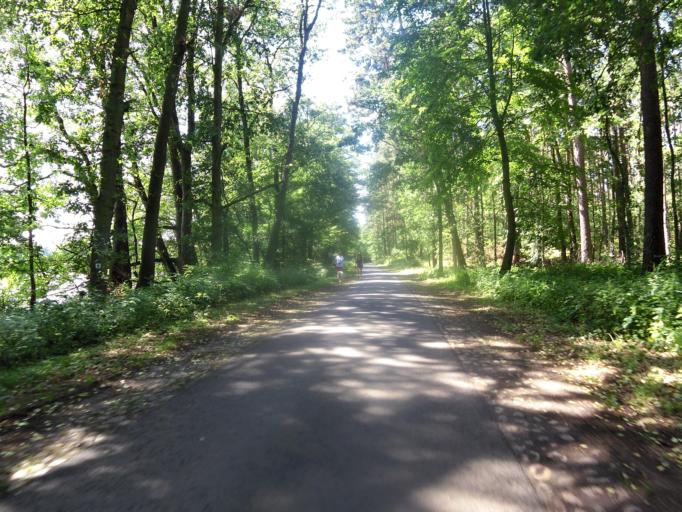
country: DE
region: Brandenburg
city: Lychen
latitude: 53.1886
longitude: 13.2324
